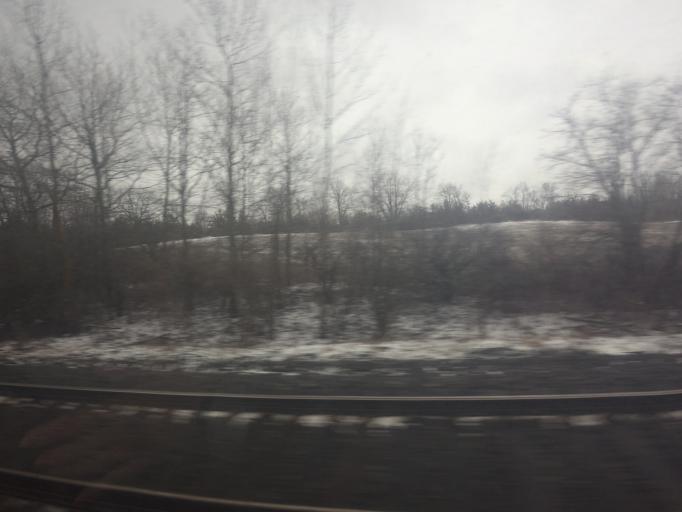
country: CA
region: Ontario
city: Deseronto
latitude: 44.2104
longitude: -77.2016
